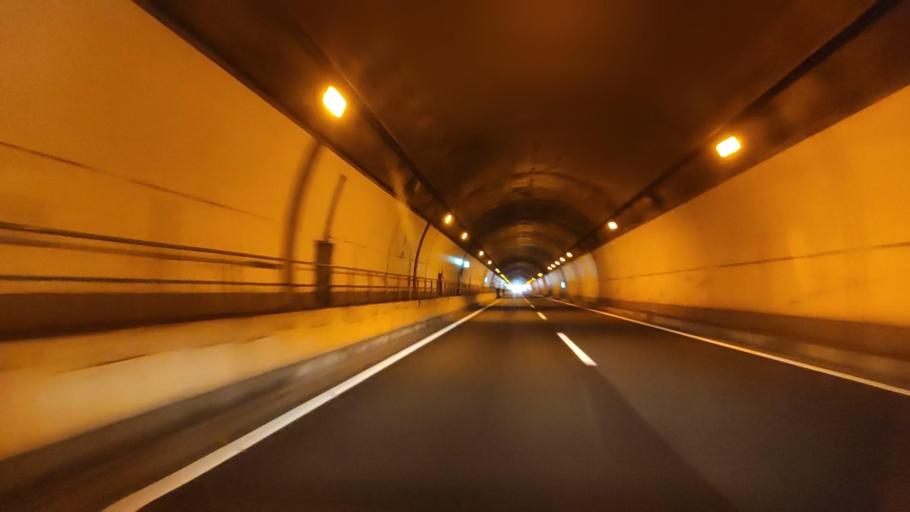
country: JP
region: Akita
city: Hanawa
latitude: 40.0117
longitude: 140.9879
